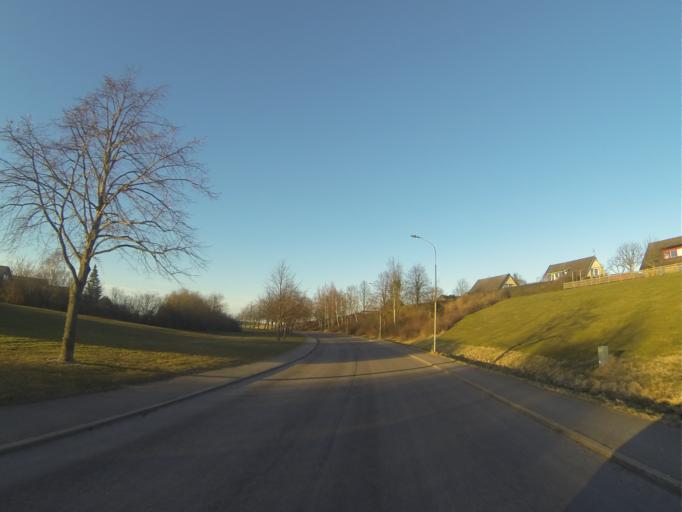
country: SE
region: Skane
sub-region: Staffanstorps Kommun
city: Staffanstorp
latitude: 55.5862
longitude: 13.1829
